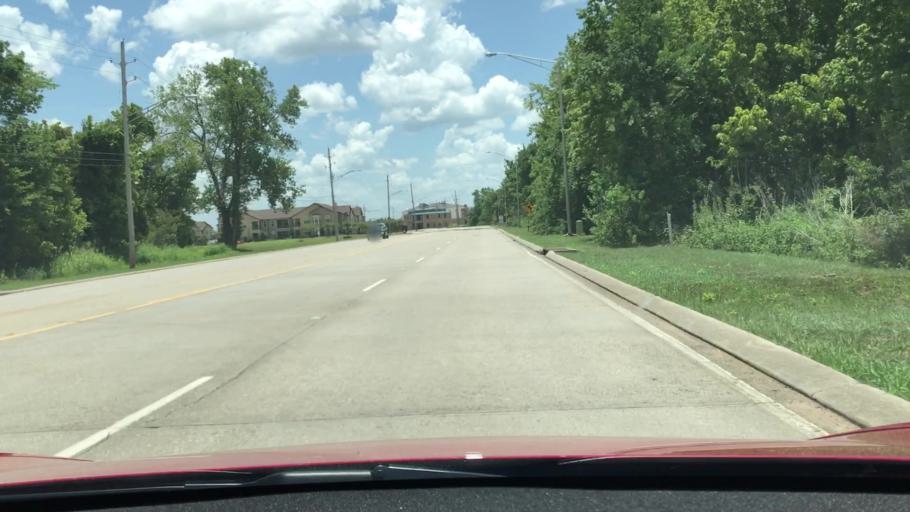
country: US
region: Louisiana
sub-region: Bossier Parish
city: Bossier City
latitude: 32.4292
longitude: -93.7255
